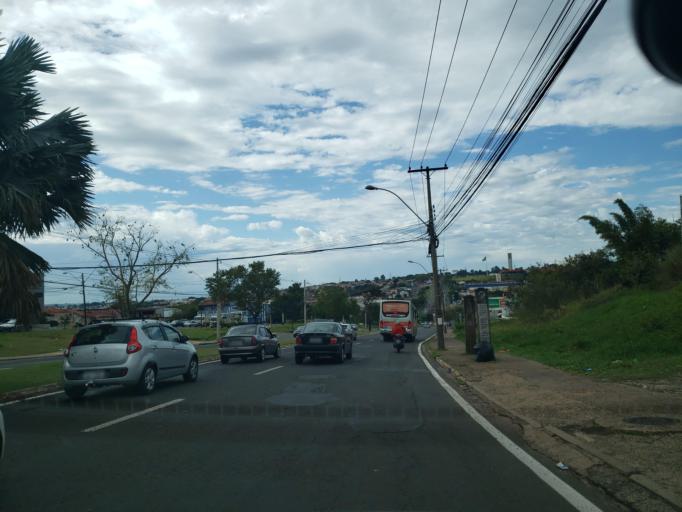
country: BR
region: Sao Paulo
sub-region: Bauru
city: Bauru
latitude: -22.3384
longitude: -49.0441
